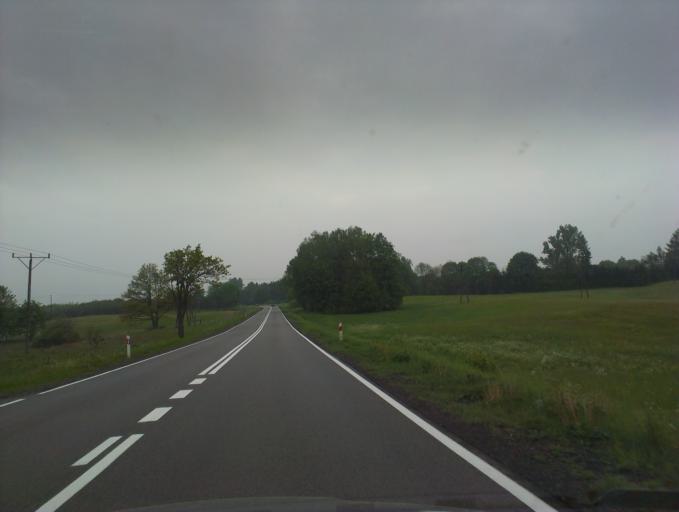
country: PL
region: West Pomeranian Voivodeship
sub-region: Powiat koszalinski
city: Bobolice
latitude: 53.9002
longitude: 16.6124
